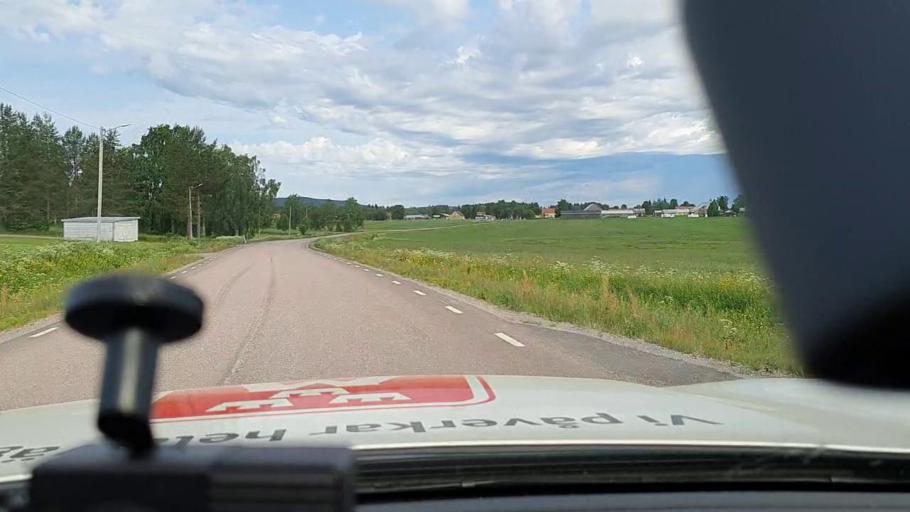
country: SE
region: Norrbotten
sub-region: Bodens Kommun
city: Saevast
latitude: 65.7047
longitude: 21.7672
